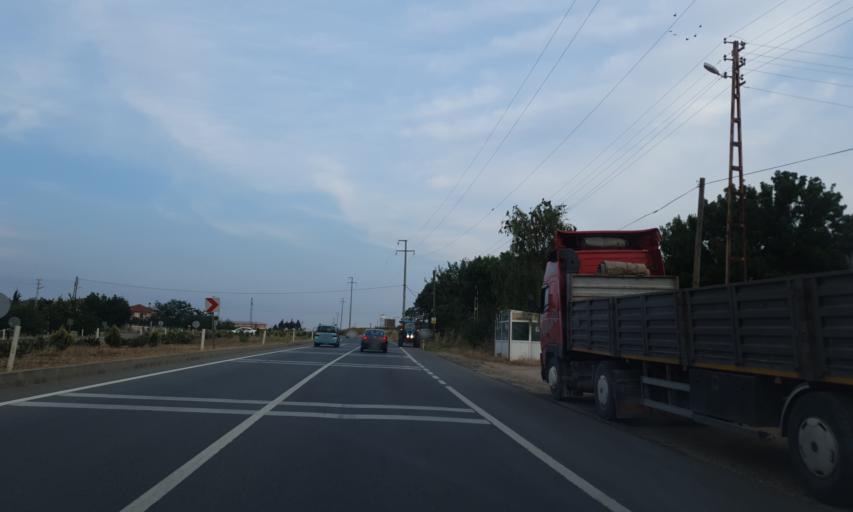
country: TR
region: Kirklareli
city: Luleburgaz
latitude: 41.3599
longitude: 27.4204
